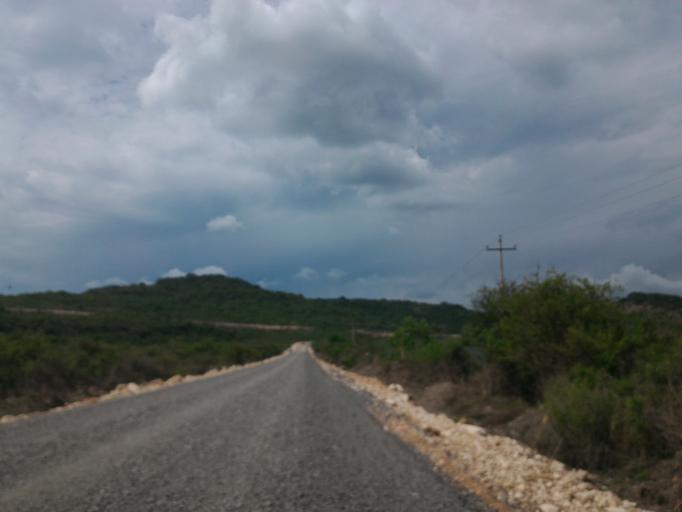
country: MX
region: Jalisco
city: San Diego de Alejandria
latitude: 20.9122
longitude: -102.0449
